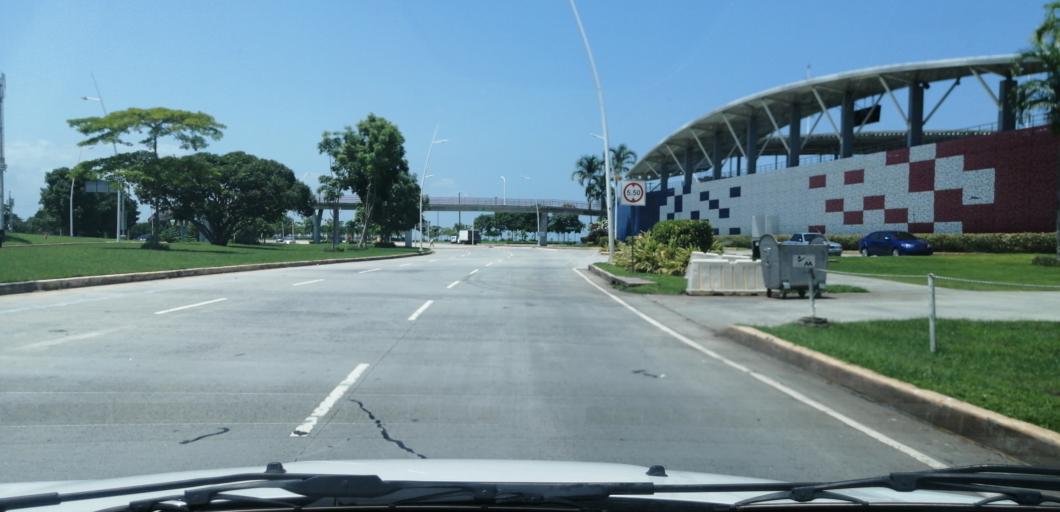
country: PA
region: Panama
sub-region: Distrito de Panama
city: Ancon
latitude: 8.9468
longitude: -79.5501
